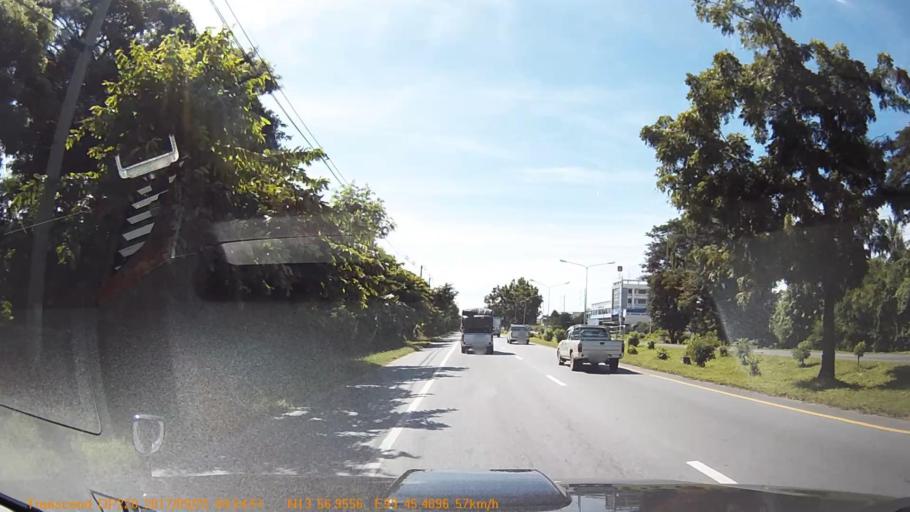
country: TH
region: Kanchanaburi
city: Tha Maka
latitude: 13.9489
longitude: 99.7583
